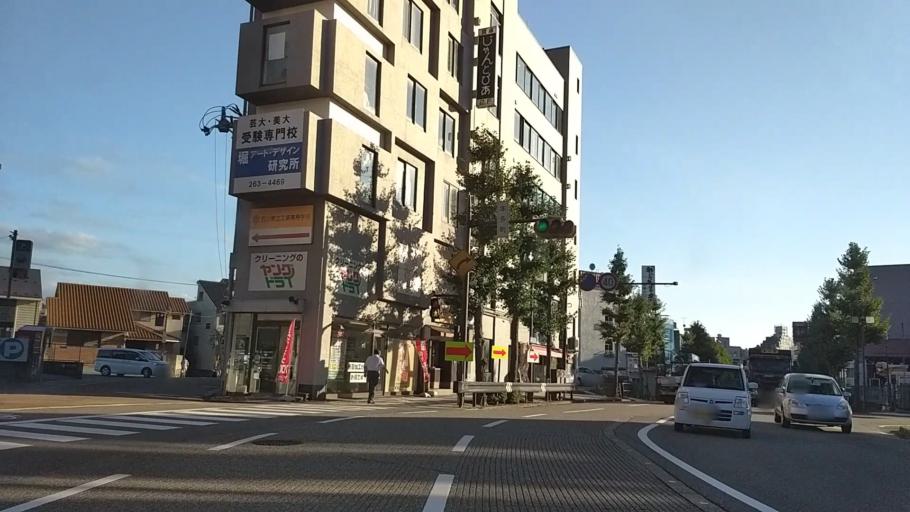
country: JP
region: Ishikawa
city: Nonoichi
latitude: 36.5578
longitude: 136.6593
